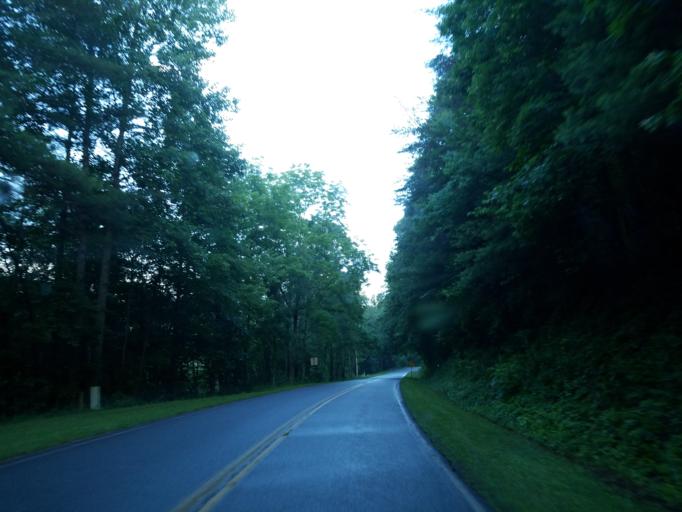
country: US
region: Georgia
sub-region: Fannin County
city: Blue Ridge
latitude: 34.7184
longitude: -84.2311
